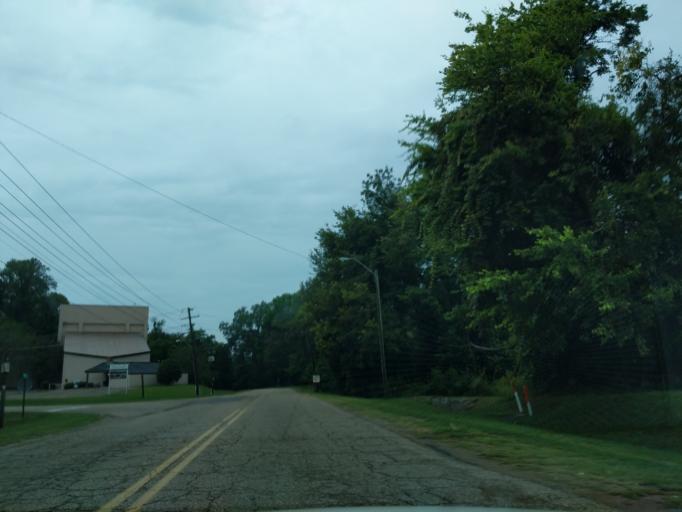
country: US
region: Mississippi
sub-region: Warren County
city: Vicksburg
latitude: 32.3177
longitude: -90.8891
